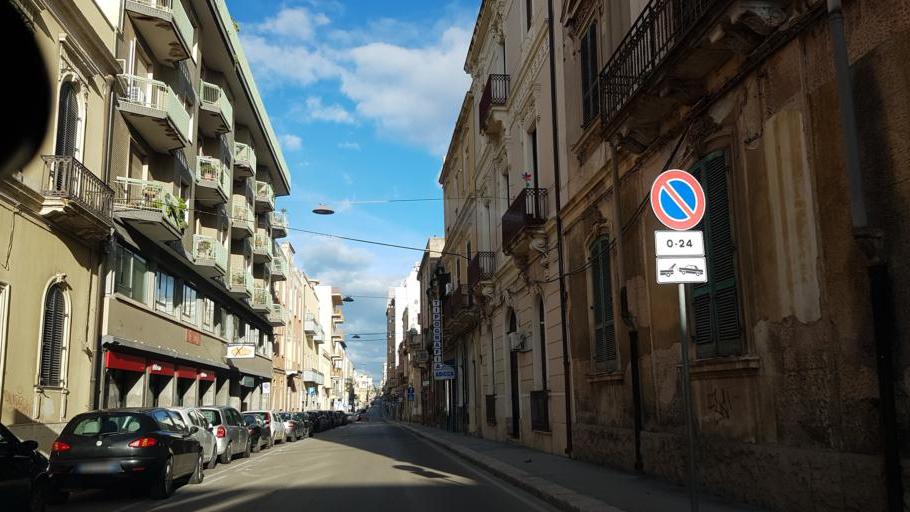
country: IT
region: Apulia
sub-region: Provincia di Brindisi
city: Brindisi
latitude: 40.6333
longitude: 17.9416
